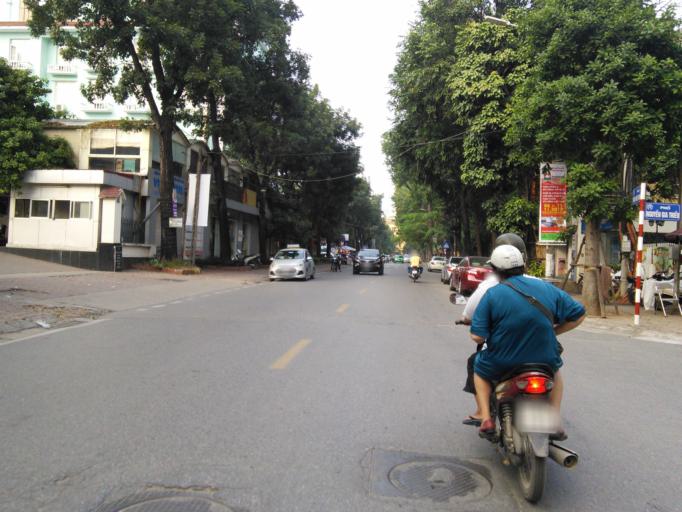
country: VN
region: Ha Noi
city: Hanoi
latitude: 21.0204
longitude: 105.8446
